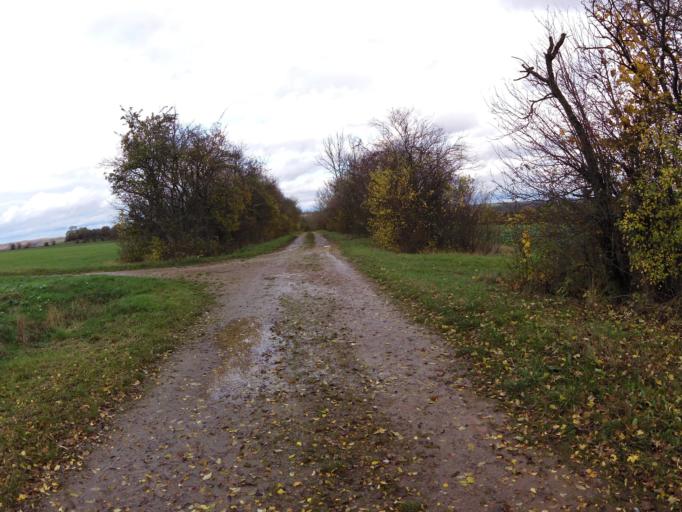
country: DE
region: Thuringia
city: Ifta
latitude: 51.0575
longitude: 10.1315
